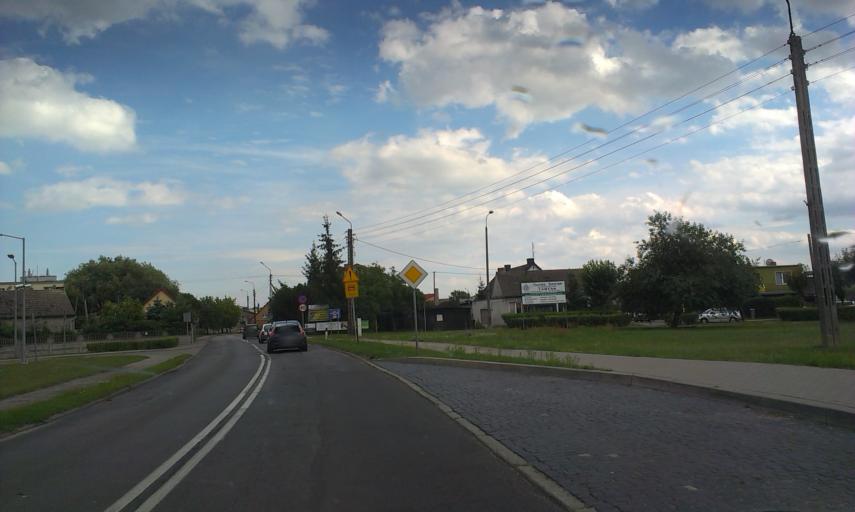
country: PL
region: Greater Poland Voivodeship
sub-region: Powiat zlotowski
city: Krajenka
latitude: 53.3012
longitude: 16.9882
